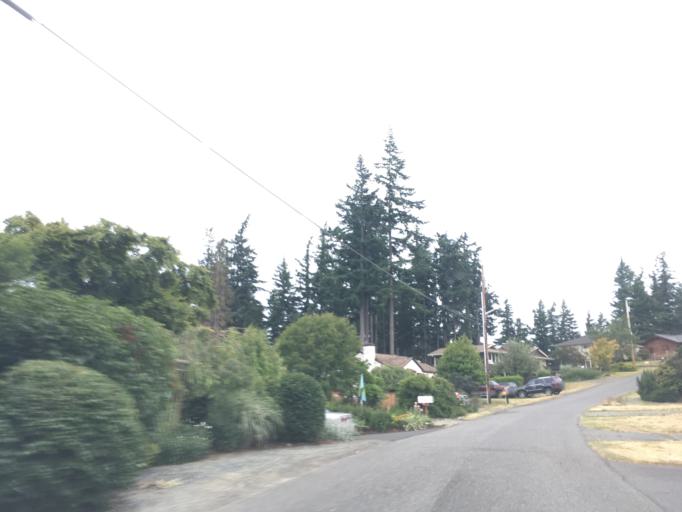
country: US
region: Washington
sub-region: Whatcom County
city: Bellingham
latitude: 48.7120
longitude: -122.5025
